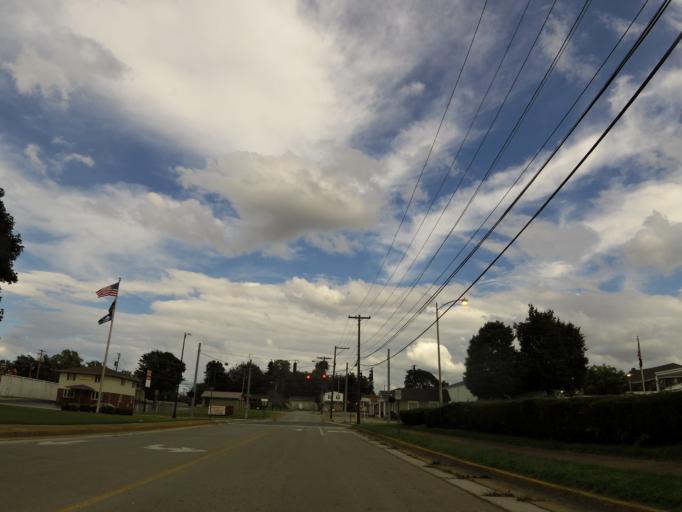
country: US
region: Kentucky
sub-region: Christian County
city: Hopkinsville
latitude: 36.8704
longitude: -87.4865
